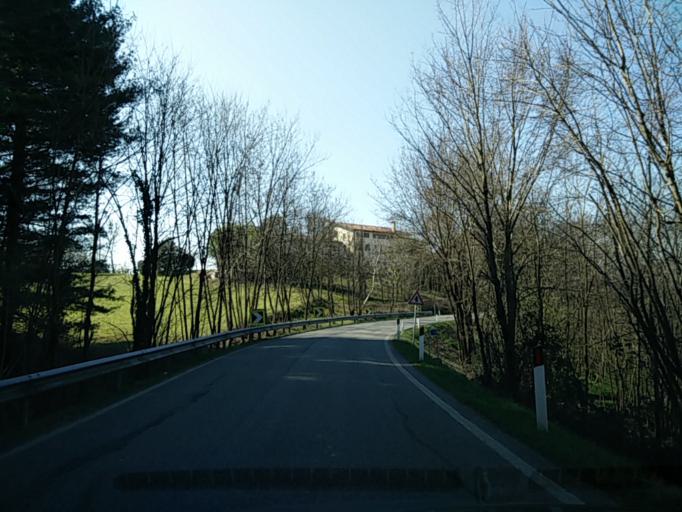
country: IT
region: Veneto
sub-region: Provincia di Treviso
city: Sernaglia della Battaglia
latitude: 45.8468
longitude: 12.1539
